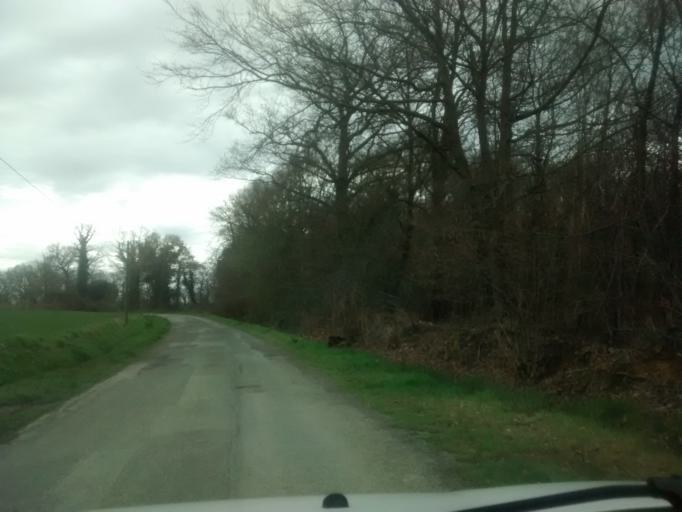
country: FR
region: Brittany
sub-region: Departement d'Ille-et-Vilaine
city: Fouillard
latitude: 48.1675
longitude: -1.6053
